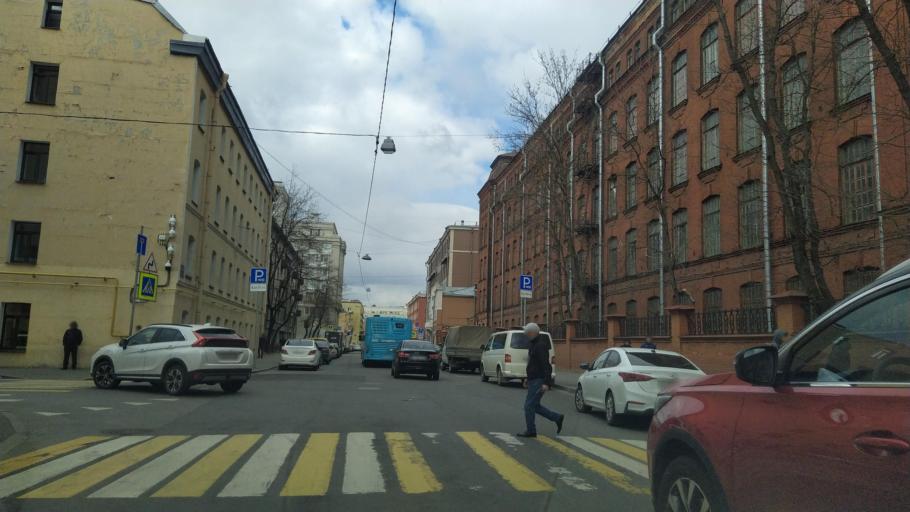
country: RU
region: St.-Petersburg
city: Centralniy
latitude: 59.9390
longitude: 30.3939
